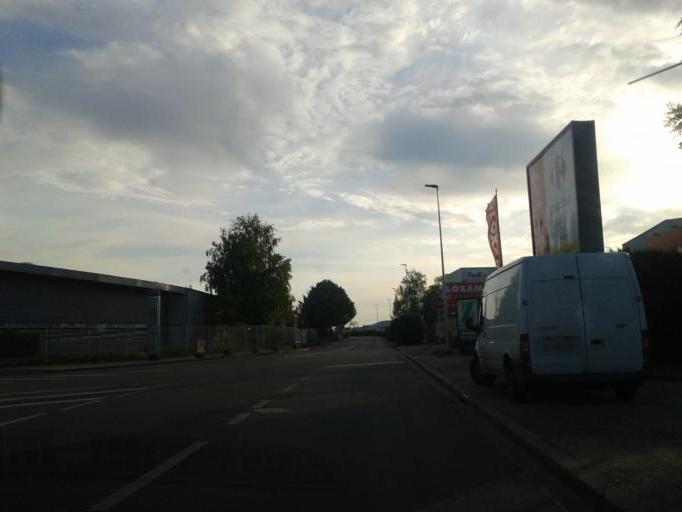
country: FR
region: Centre
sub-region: Departement du Loiret
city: Saint-Jean-de-la-Ruelle
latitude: 47.9021
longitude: 1.8550
